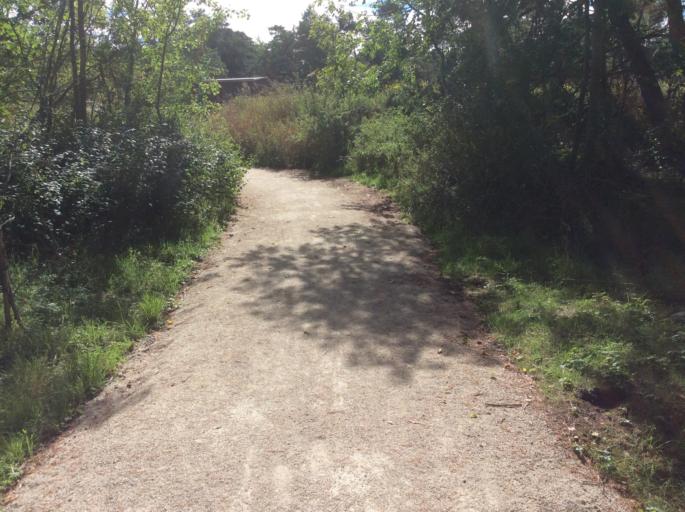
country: SE
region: Gotland
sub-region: Gotland
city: Vibble
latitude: 57.6184
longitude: 18.2683
